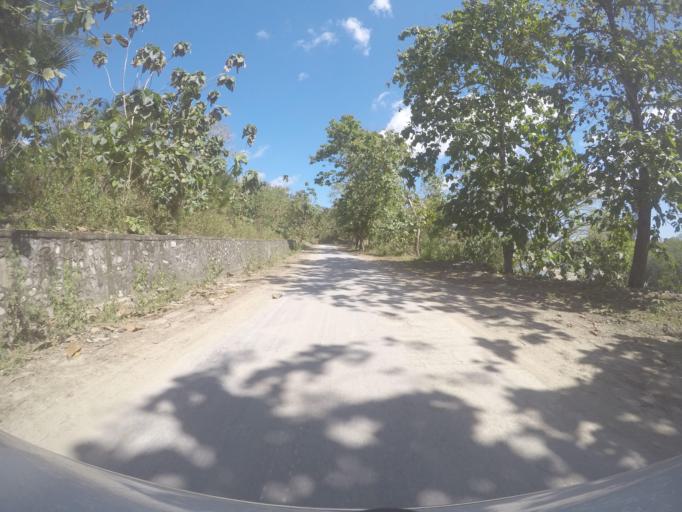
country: TL
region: Viqueque
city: Viqueque
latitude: -8.9026
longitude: 126.3929
